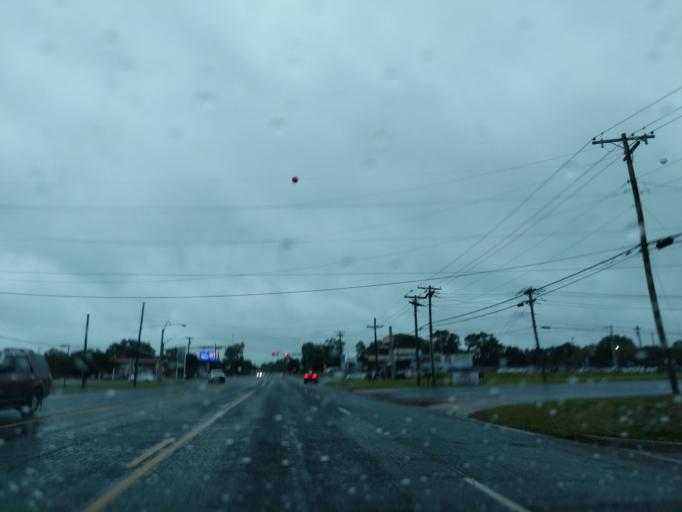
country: US
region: Texas
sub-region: Nacogdoches County
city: Nacogdoches
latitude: 31.6510
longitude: -94.6557
